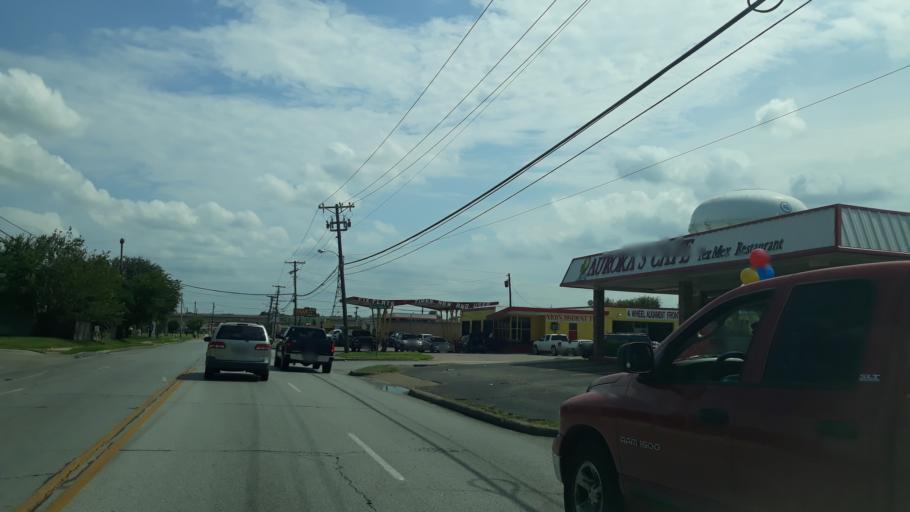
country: US
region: Texas
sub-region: Dallas County
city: Irving
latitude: 32.8183
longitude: -96.9764
